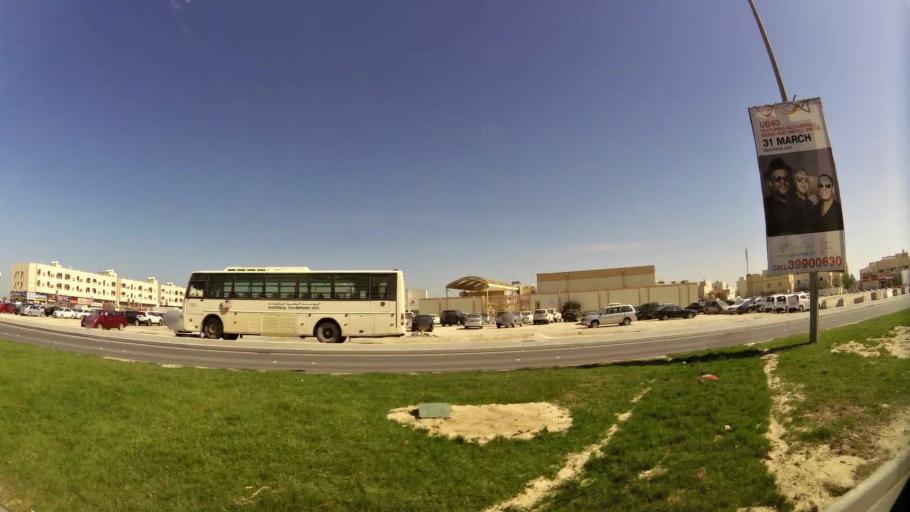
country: BH
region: Muharraq
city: Al Hadd
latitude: 26.2593
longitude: 50.6391
